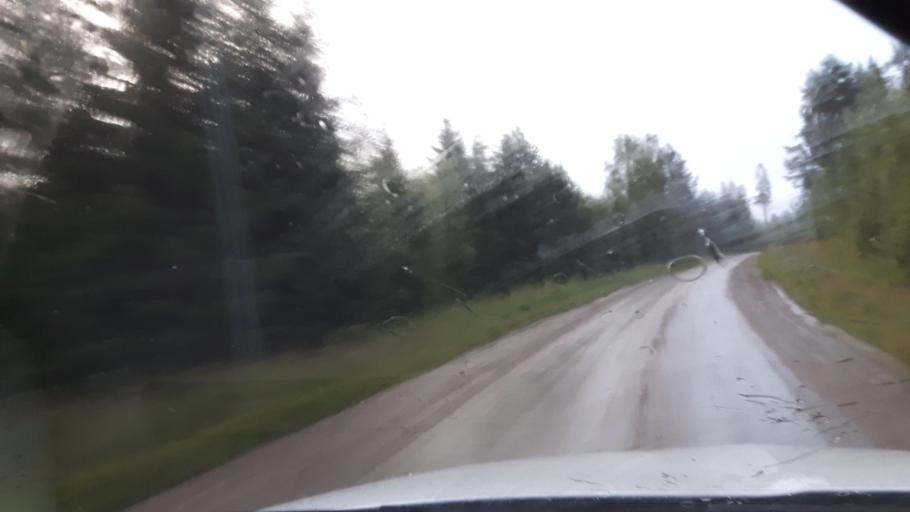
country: SE
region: Vaesternorrland
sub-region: Ange Kommun
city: Ange
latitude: 62.1438
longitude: 15.6613
